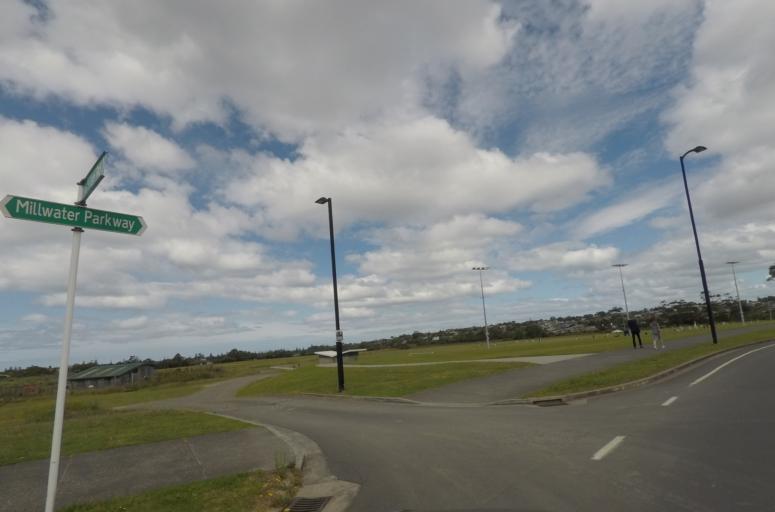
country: NZ
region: Auckland
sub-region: Auckland
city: Rothesay Bay
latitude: -36.5988
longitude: 174.6784
